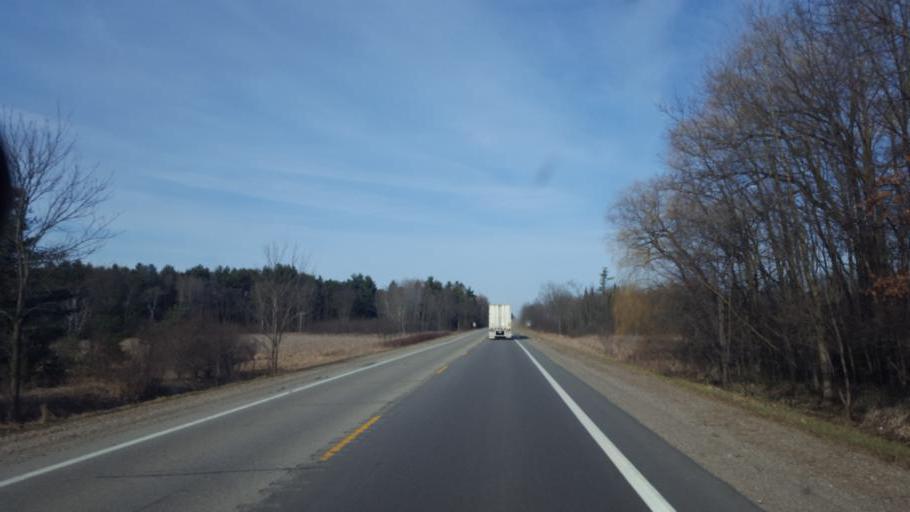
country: US
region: Michigan
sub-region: Montcalm County
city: Lakeview
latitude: 43.4309
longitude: -85.2198
